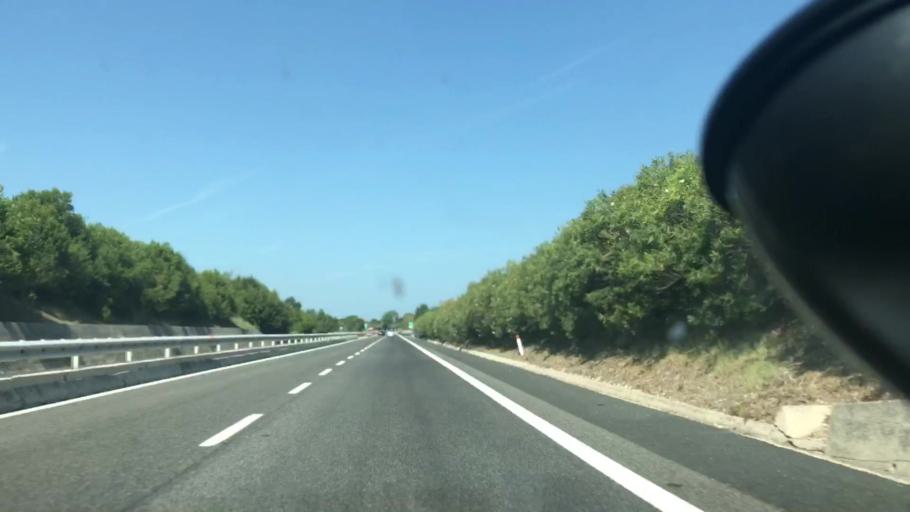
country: IT
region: Abruzzo
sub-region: Provincia di Chieti
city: Tollo
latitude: 42.3520
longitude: 14.3535
